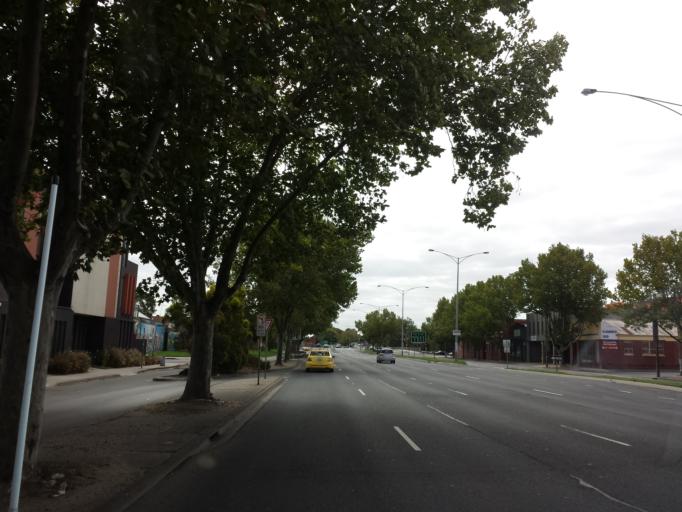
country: AU
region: Victoria
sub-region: Yarra
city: Clifton Hill
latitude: -37.7976
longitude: 144.9933
